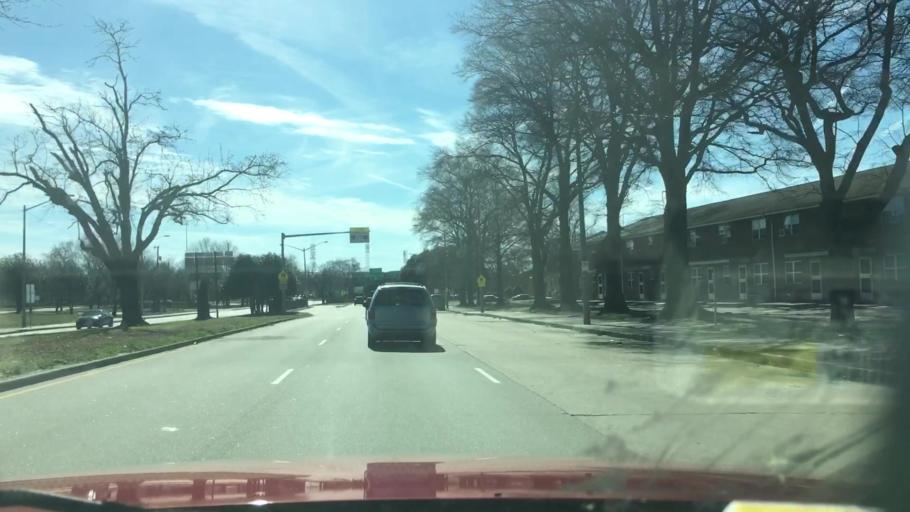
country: US
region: Virginia
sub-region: City of Norfolk
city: Norfolk
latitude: 36.8490
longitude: -76.2769
